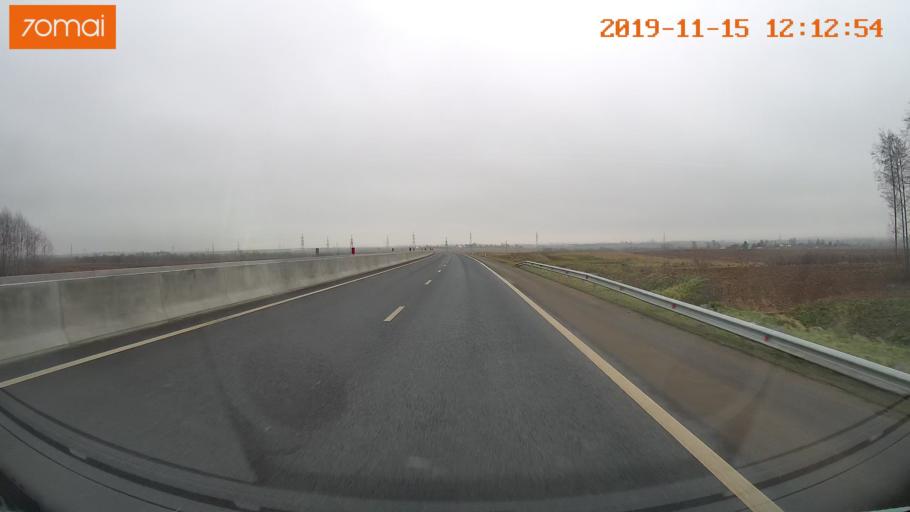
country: RU
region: Vologda
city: Vologda
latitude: 59.1701
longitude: 39.7753
